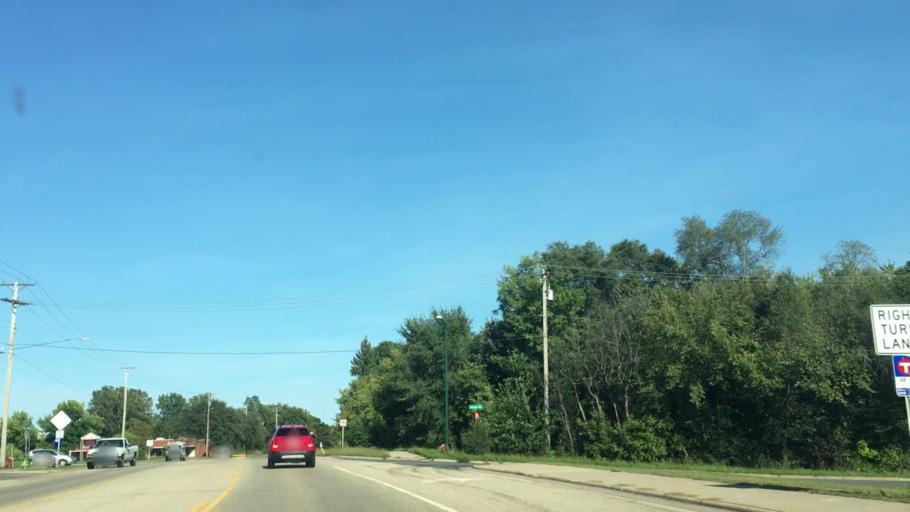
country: US
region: Minnesota
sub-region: Dakota County
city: South Saint Paul
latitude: 44.8838
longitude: -93.0683
